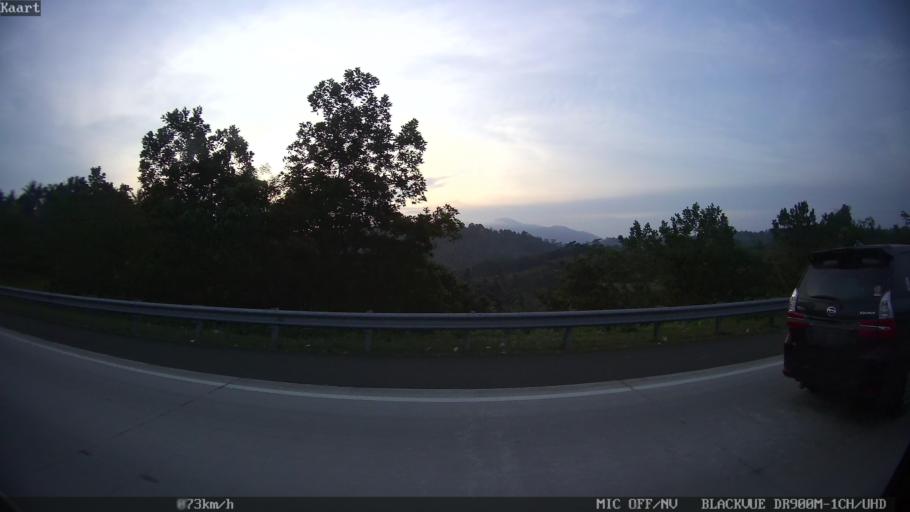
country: ID
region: Lampung
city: Penengahan
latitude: -5.8387
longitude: 105.7294
